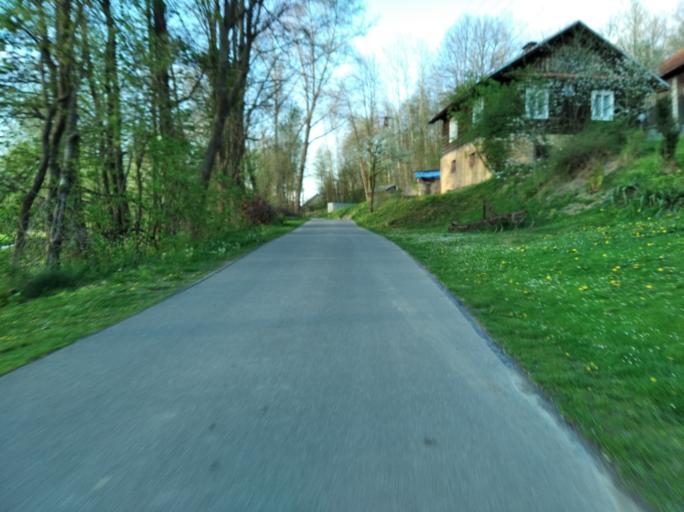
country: PL
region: Subcarpathian Voivodeship
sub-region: Powiat strzyzowski
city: Wysoka Strzyzowska
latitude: 49.8519
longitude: 21.7349
